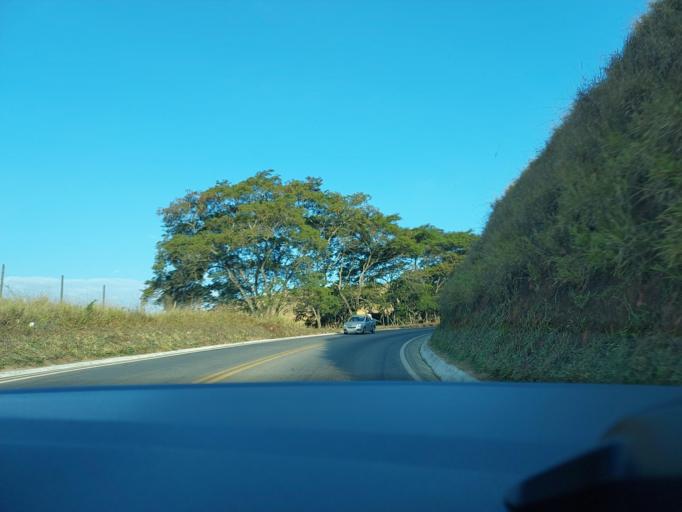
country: BR
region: Minas Gerais
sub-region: Muriae
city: Muriae
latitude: -21.1213
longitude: -42.4034
